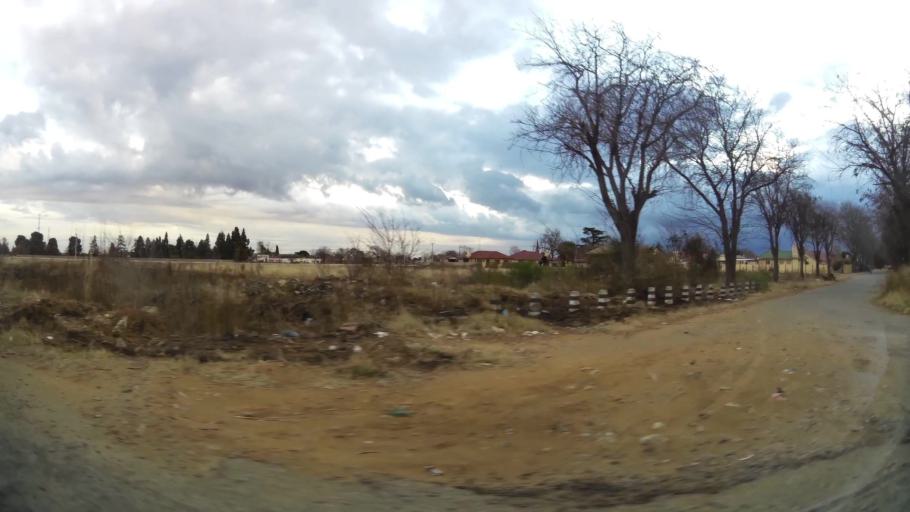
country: ZA
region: Orange Free State
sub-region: Lejweleputswa District Municipality
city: Welkom
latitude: -27.9678
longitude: 26.7744
